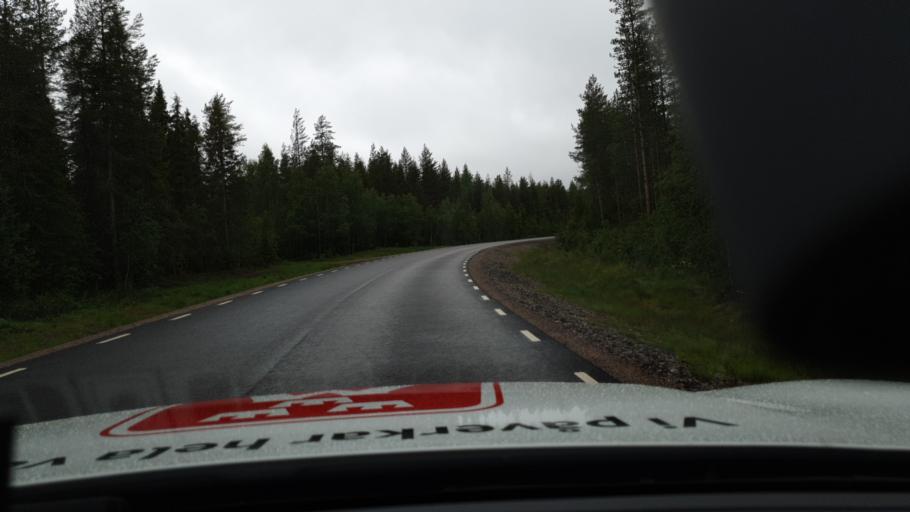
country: SE
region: Norrbotten
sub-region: Overtornea Kommun
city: OEvertornea
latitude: 66.4265
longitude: 23.5336
